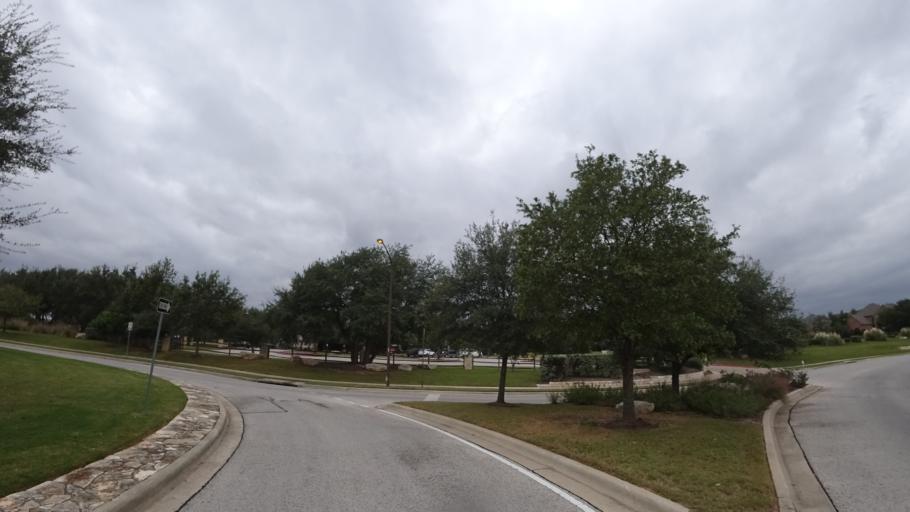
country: US
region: Texas
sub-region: Travis County
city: Bee Cave
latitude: 30.3448
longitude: -97.9100
